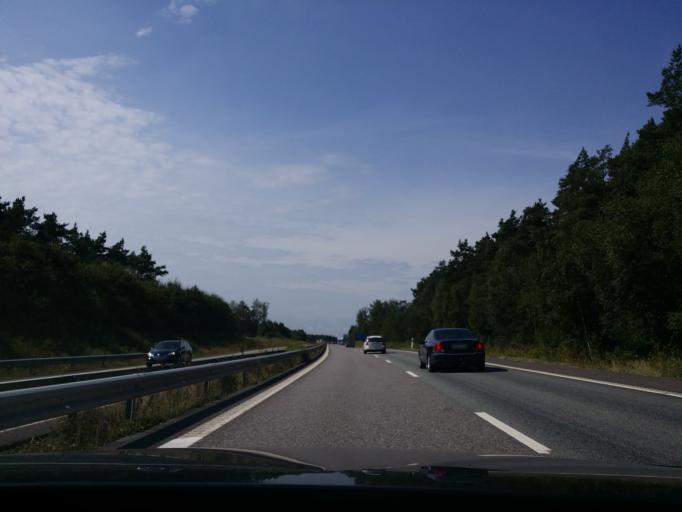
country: SE
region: Blekinge
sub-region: Solvesborgs Kommun
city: Soelvesborg
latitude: 56.0698
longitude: 14.5269
